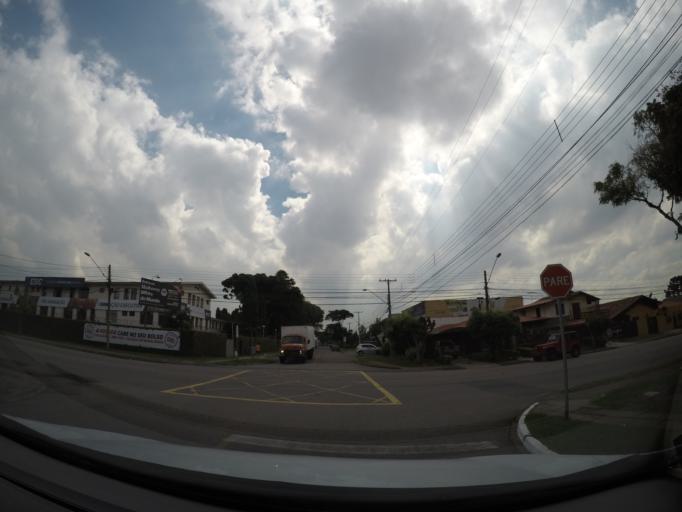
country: BR
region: Parana
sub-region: Curitiba
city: Curitiba
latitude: -25.4844
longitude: -49.2555
